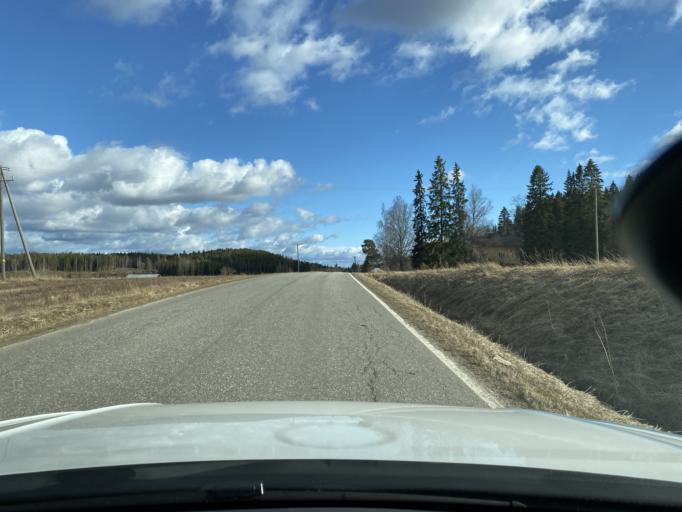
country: FI
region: Pirkanmaa
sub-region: Lounais-Pirkanmaa
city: Punkalaidun
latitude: 61.0822
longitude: 23.1616
